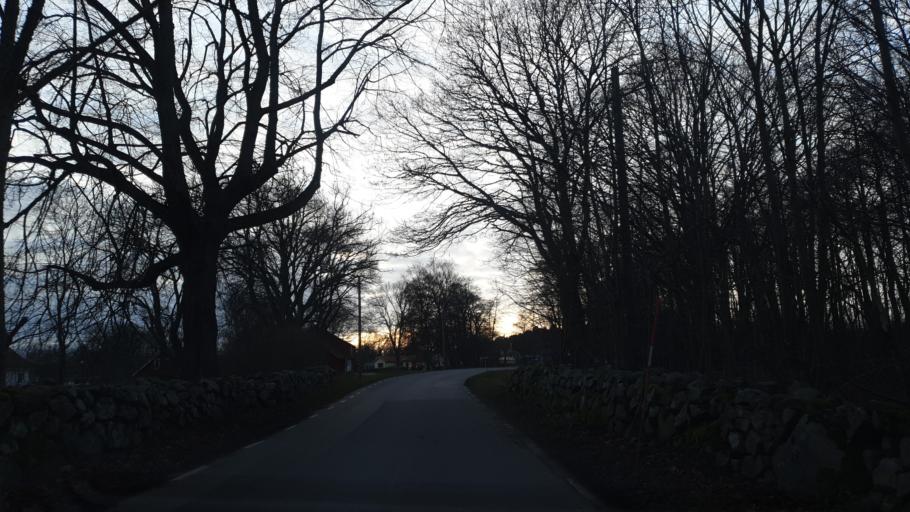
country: SE
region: Blekinge
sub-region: Karlskrona Kommun
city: Jaemjoe
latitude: 56.1665
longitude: 15.9252
